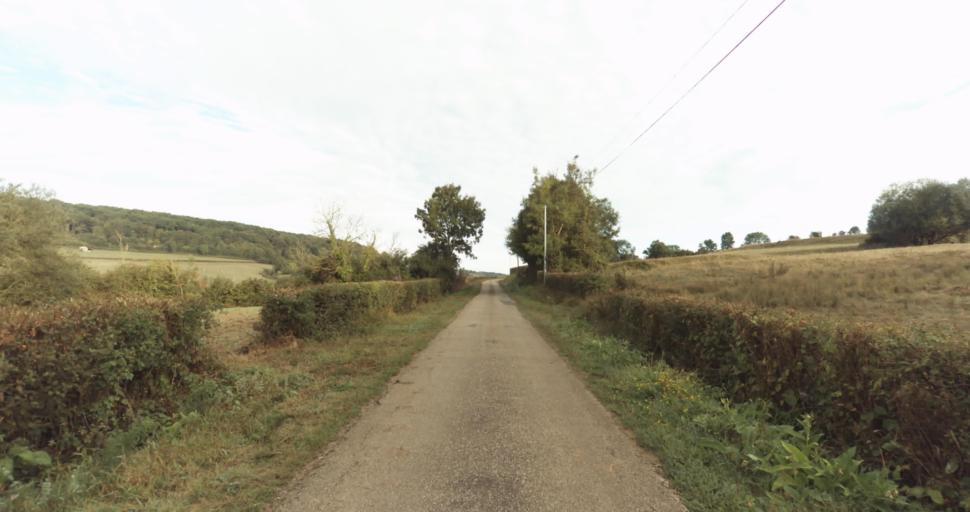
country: FR
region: Lower Normandy
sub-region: Departement de l'Orne
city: Vimoutiers
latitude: 48.9005
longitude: 0.2165
